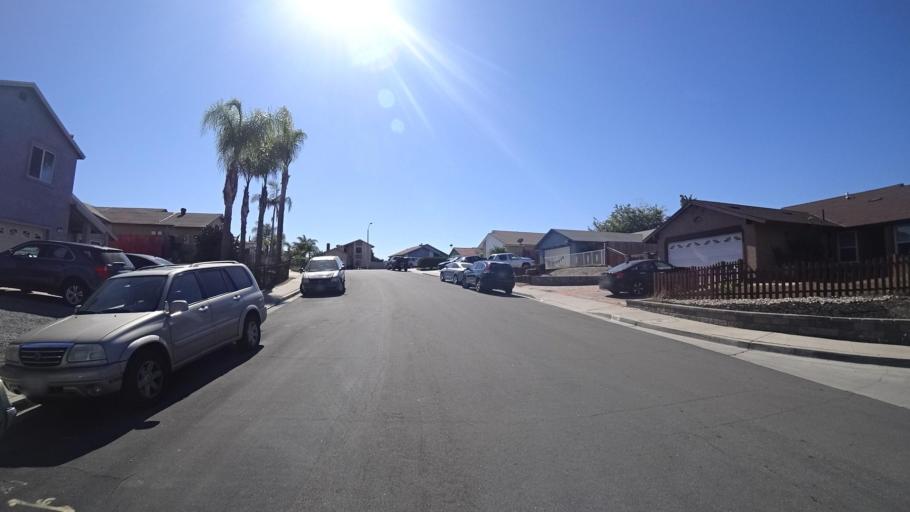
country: US
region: California
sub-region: San Diego County
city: La Presa
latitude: 32.7032
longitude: -117.0227
